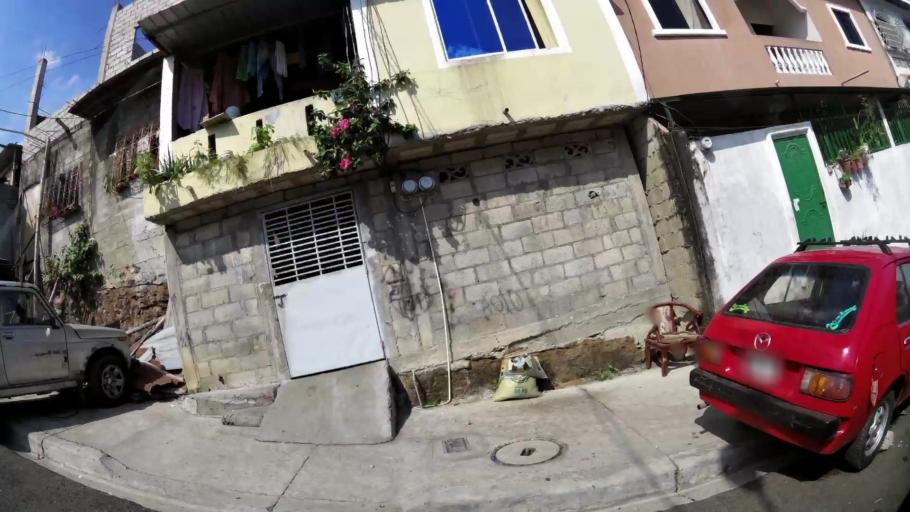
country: EC
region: Guayas
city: Guayaquil
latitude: -2.1497
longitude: -79.9410
